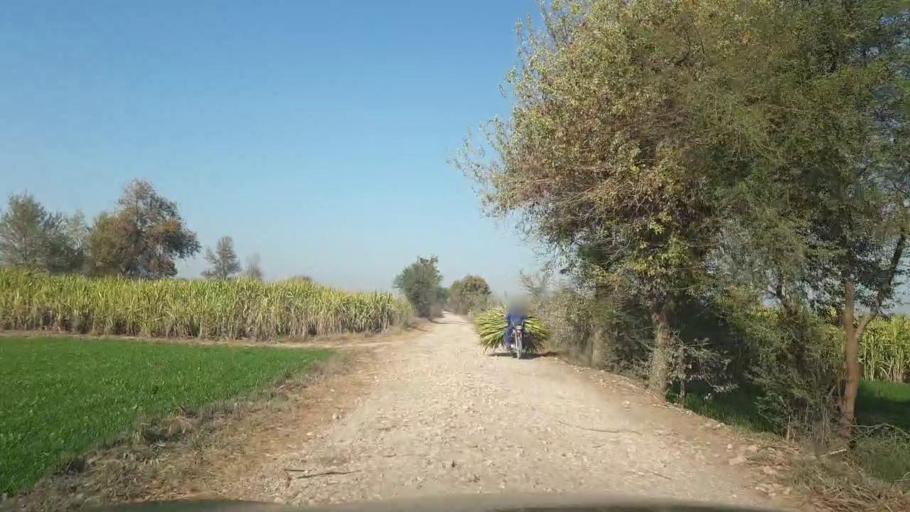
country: PK
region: Sindh
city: Mirpur Mathelo
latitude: 27.9966
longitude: 69.4794
